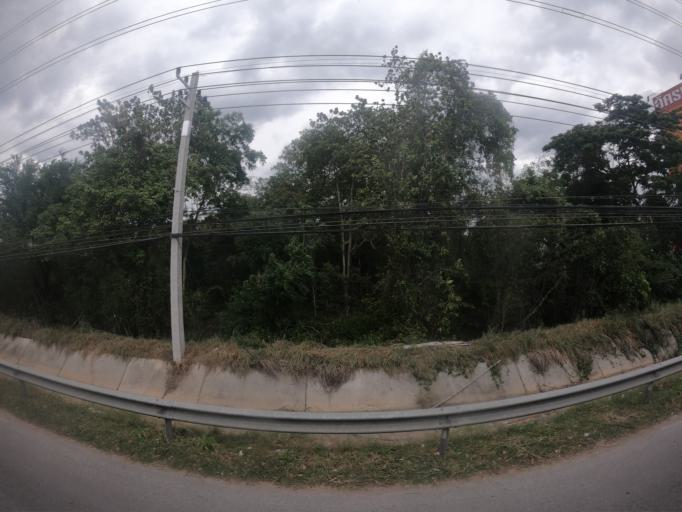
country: TH
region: Nakhon Ratchasima
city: Nakhon Ratchasima
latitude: 14.9373
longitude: 102.1337
